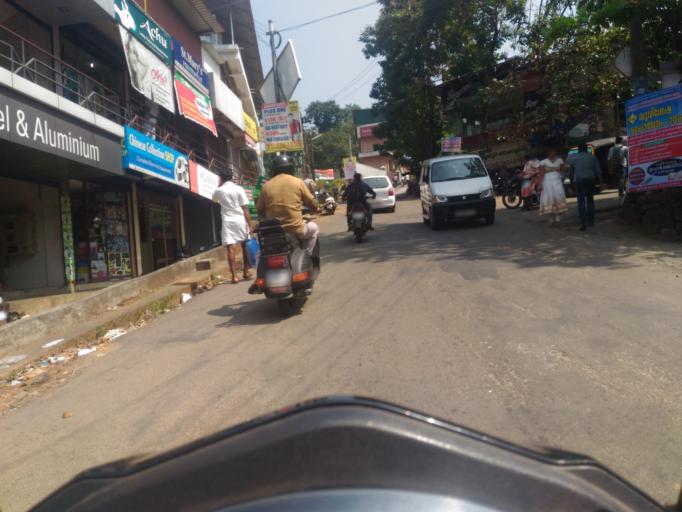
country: IN
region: Kerala
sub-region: Ernakulam
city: Muvattupula
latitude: 9.8944
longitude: 76.7077
